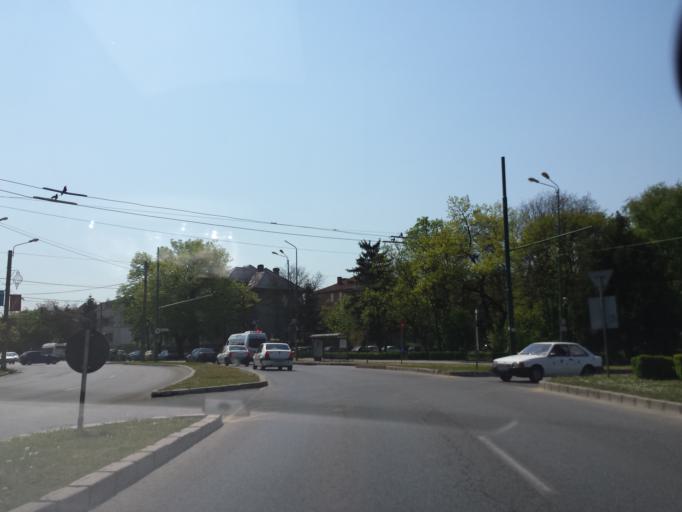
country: RO
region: Timis
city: Timisoara
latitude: 45.7533
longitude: 21.2325
